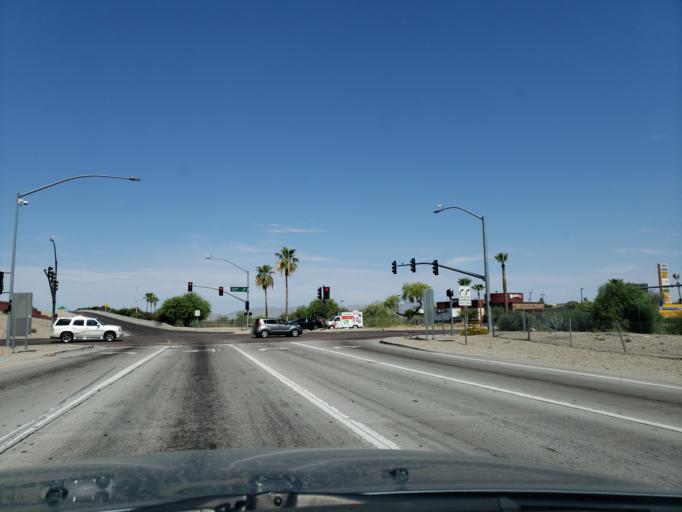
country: US
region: Arizona
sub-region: Maricopa County
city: Goodyear
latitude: 33.4585
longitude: -112.3575
